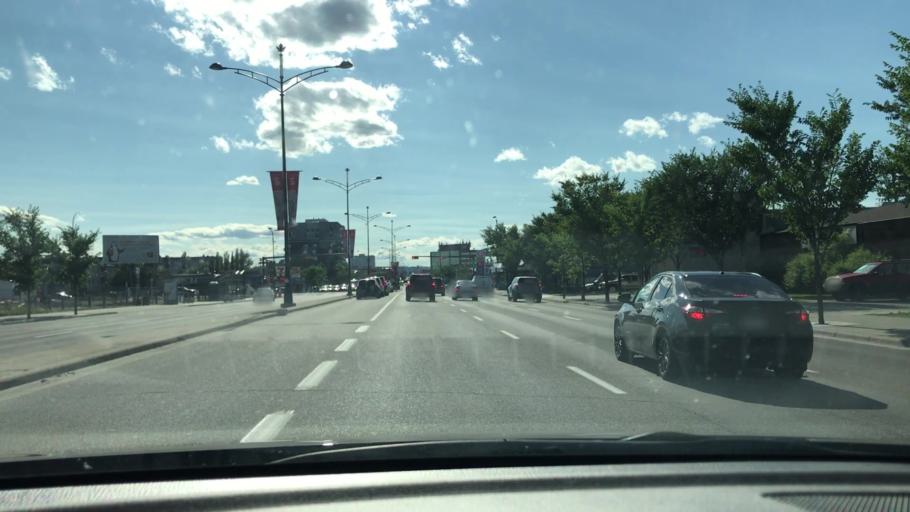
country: CA
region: Alberta
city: Calgary
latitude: 51.0670
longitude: -114.0539
